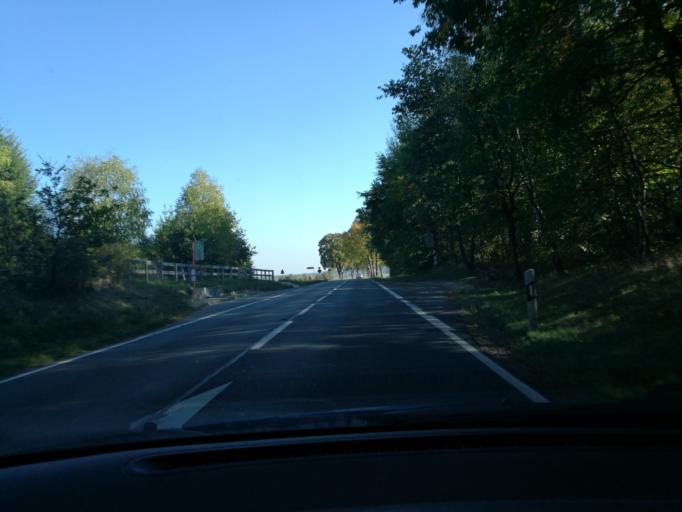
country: DE
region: Lower Saxony
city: Nahrendorf
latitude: 53.1712
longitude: 10.7794
